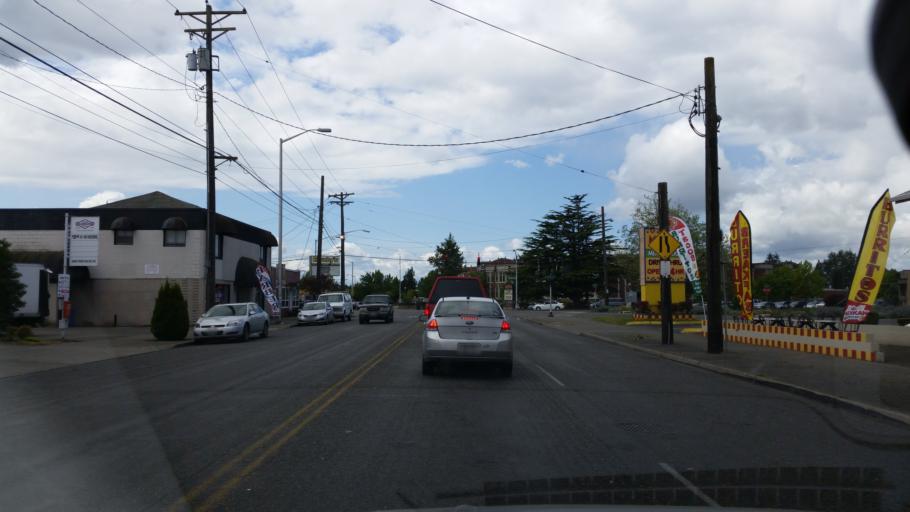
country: US
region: Washington
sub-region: Pierce County
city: Tacoma
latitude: 47.2562
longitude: -122.4614
